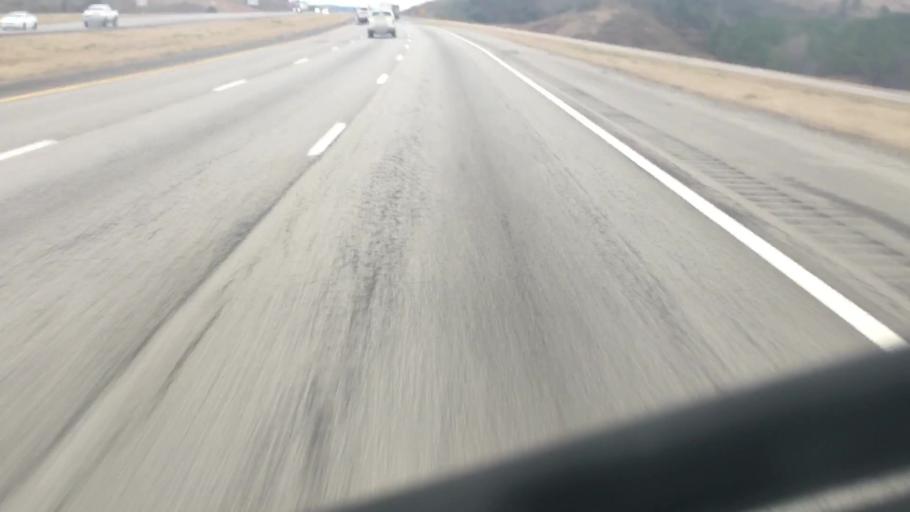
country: US
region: Alabama
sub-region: Walker County
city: Dora
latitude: 33.6798
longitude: -87.0848
